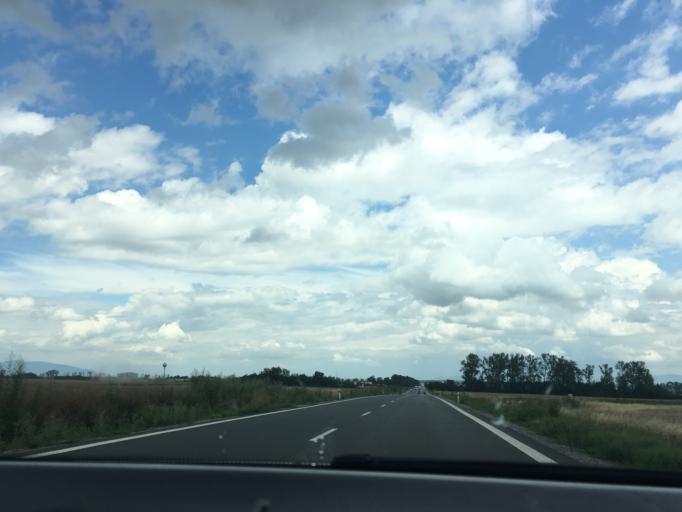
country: SK
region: Kosicky
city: Trebisov
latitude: 48.5830
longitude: 21.7075
